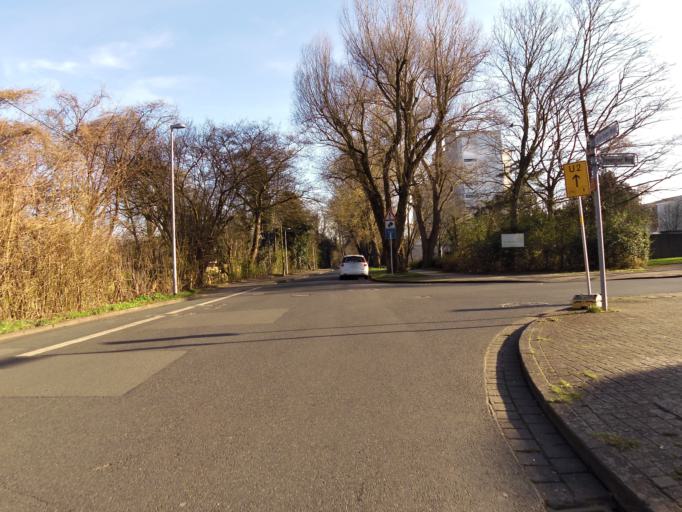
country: DE
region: Lower Saxony
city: Laatzen
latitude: 52.3792
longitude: 9.8253
